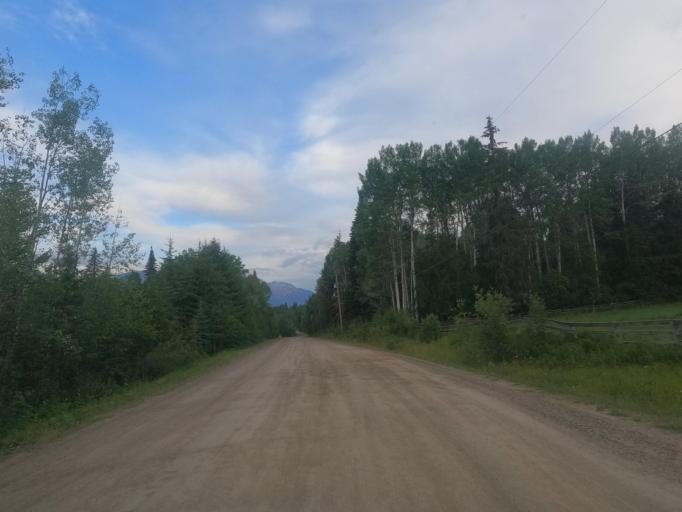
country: CA
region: British Columbia
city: Golden
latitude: 51.4457
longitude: -117.0325
